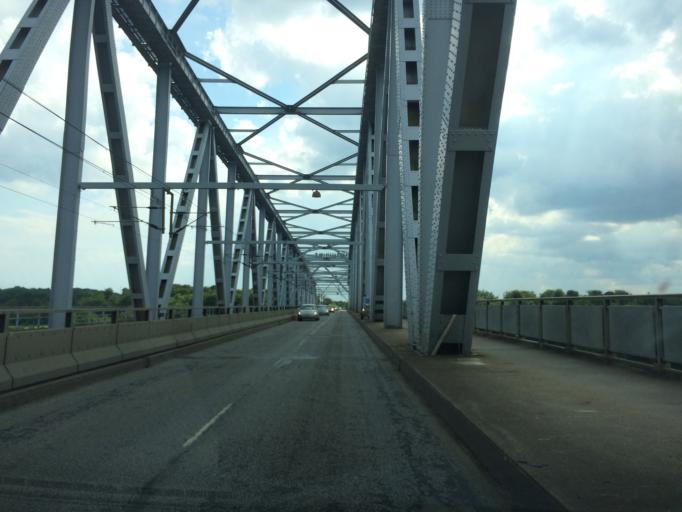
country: DK
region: South Denmark
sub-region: Fredericia Kommune
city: Snoghoj
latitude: 55.5166
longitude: 9.7086
